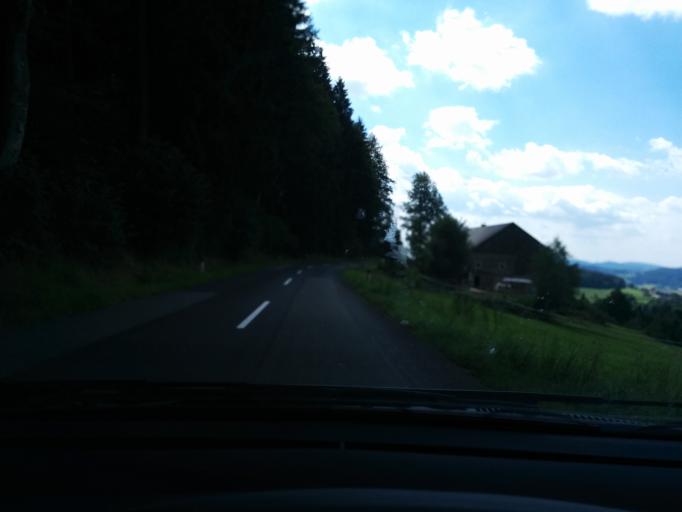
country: AT
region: Upper Austria
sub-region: Politischer Bezirk Rohrbach
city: Ulrichsberg
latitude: 48.7157
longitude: 13.8992
